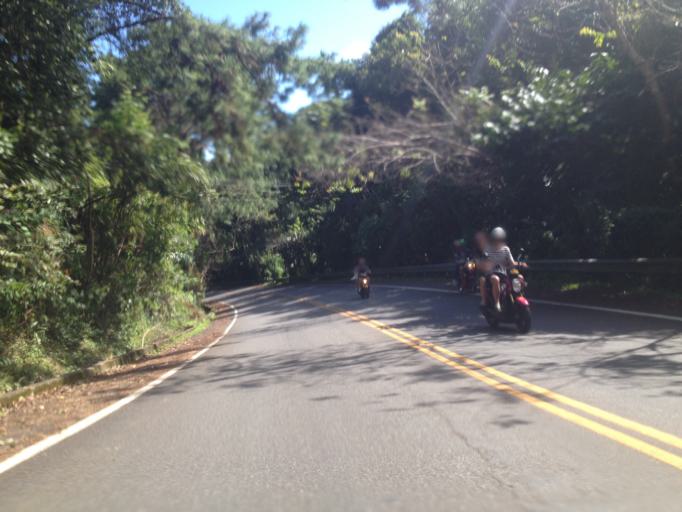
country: TH
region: Chiang Mai
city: Chiang Mai
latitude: 18.8075
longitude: 98.9136
